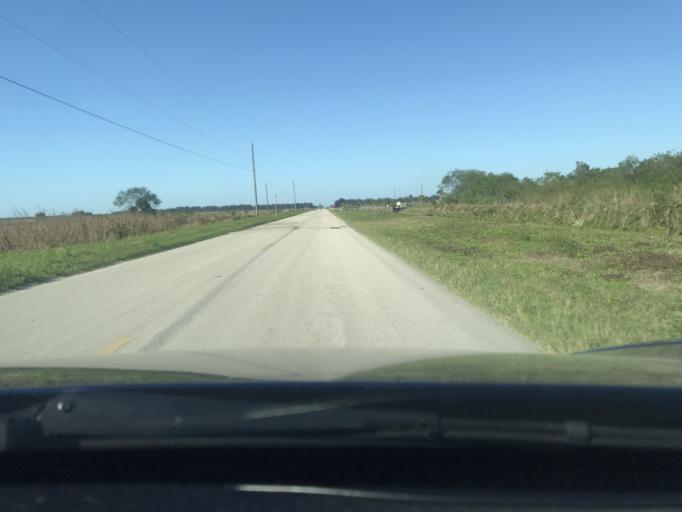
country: US
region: Florida
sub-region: Saint Lucie County
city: Fort Pierce South
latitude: 27.4092
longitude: -80.4976
